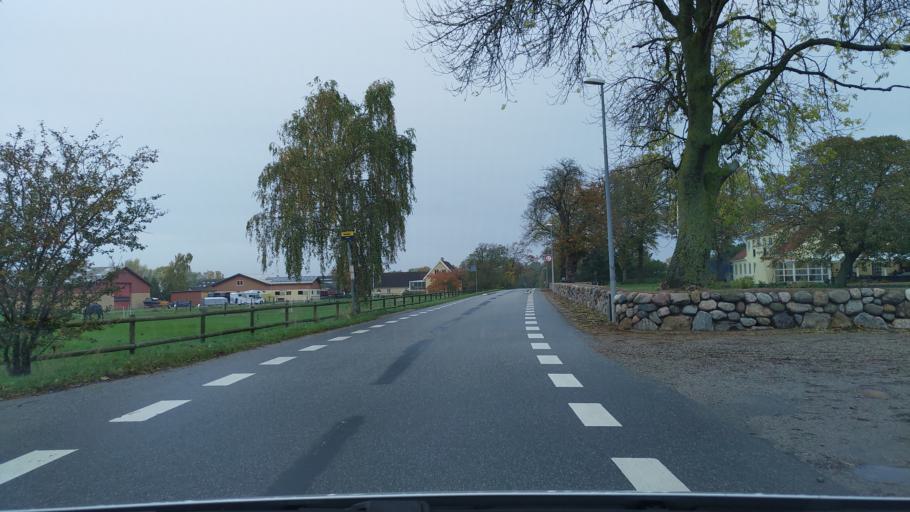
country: DK
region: Capital Region
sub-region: Tarnby Kommune
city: Tarnby
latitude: 55.5782
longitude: 12.6010
